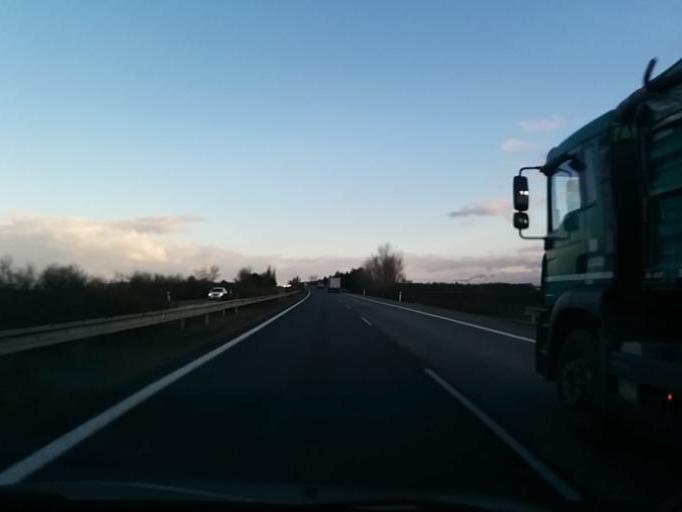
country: SK
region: Trnavsky
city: Leopoldov
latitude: 48.4158
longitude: 17.7474
